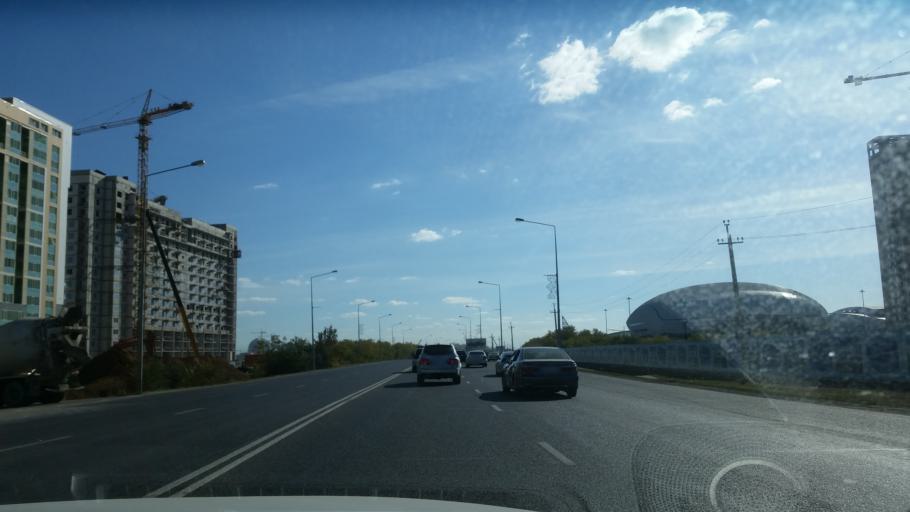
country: KZ
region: Astana Qalasy
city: Astana
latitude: 51.1148
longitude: 71.4112
